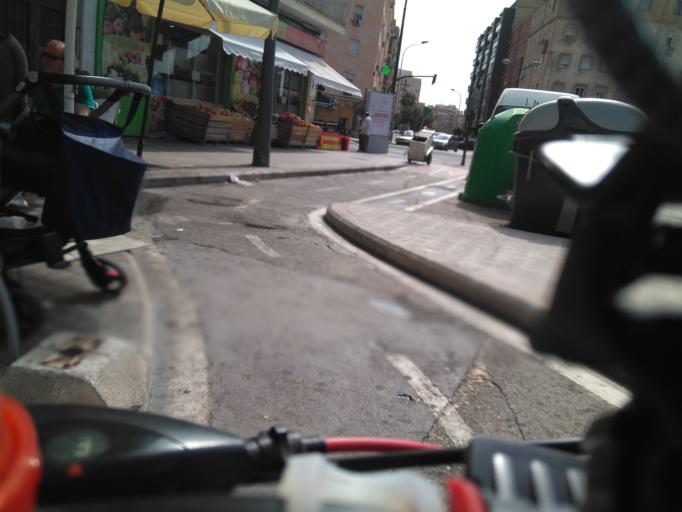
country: ES
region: Valencia
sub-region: Provincia de Valencia
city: Valencia
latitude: 39.4863
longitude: -0.3911
